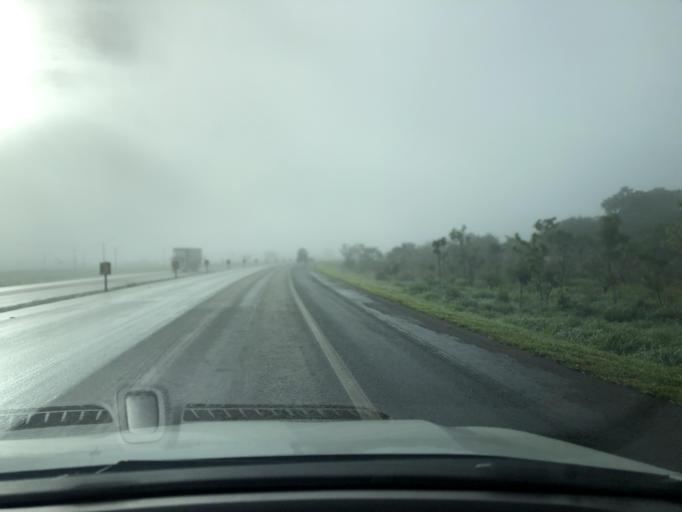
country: BR
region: Goias
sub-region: Luziania
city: Luziania
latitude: -16.2788
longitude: -47.8611
